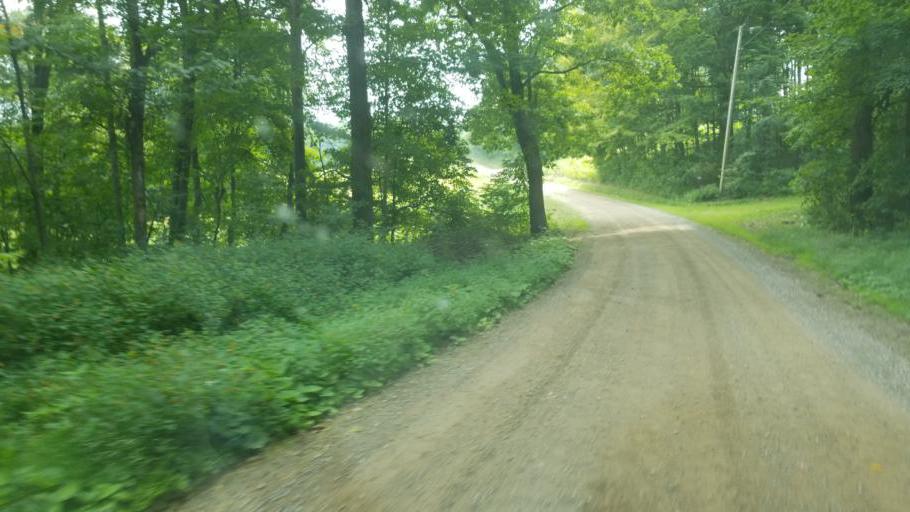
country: US
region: Ohio
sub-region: Knox County
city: Gambier
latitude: 40.4763
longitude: -82.3649
